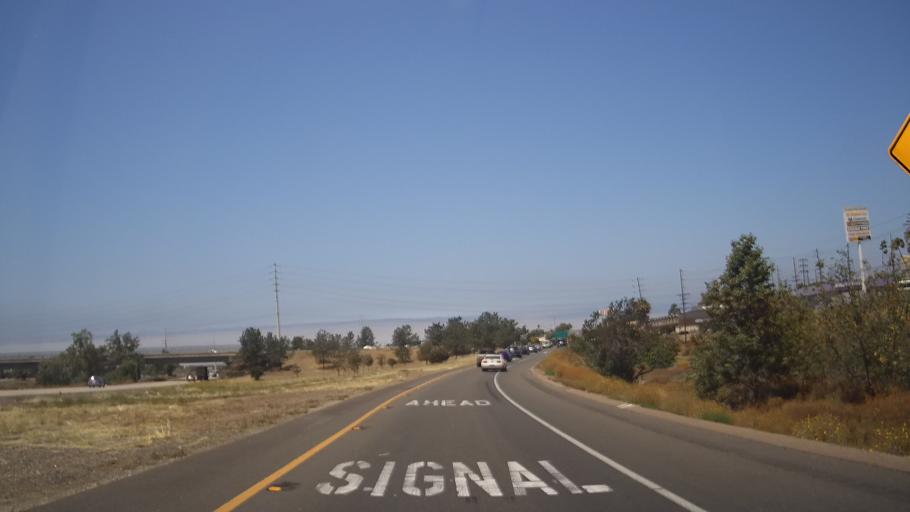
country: US
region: California
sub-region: San Diego County
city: Chula Vista
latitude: 32.6575
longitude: -117.0881
